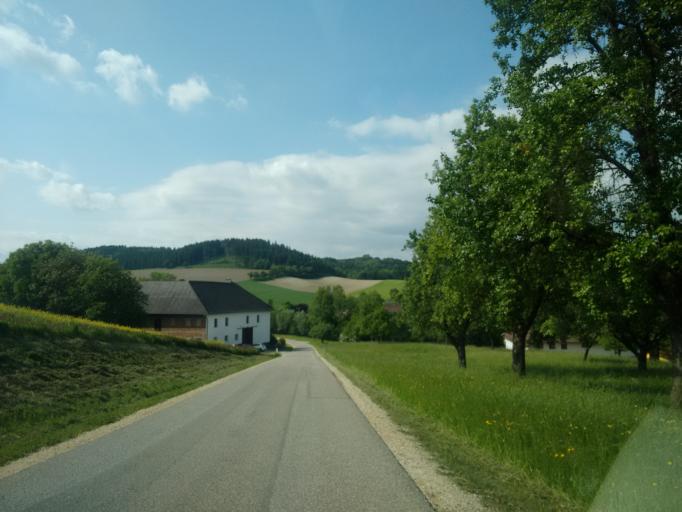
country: AT
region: Upper Austria
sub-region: Politischer Bezirk Grieskirchen
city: Bad Schallerbach
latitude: 48.1925
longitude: 13.8998
